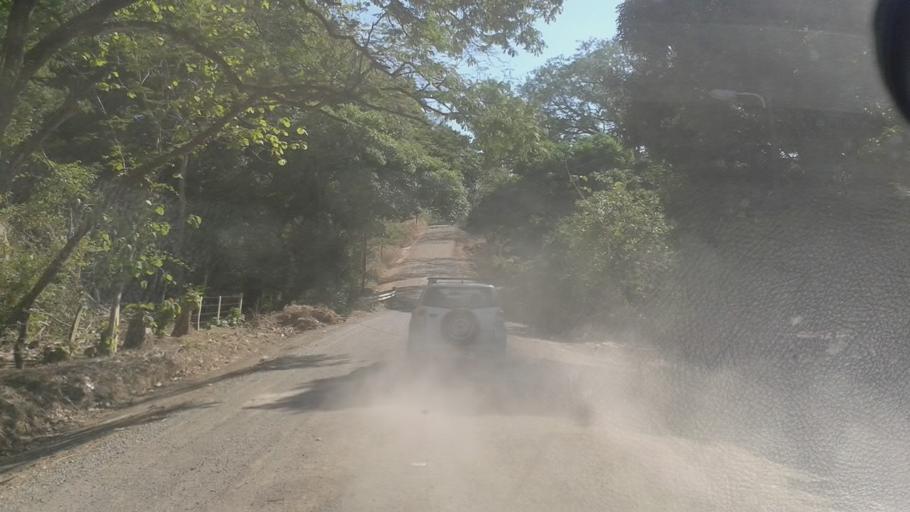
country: CR
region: Guanacaste
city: Santa Cruz
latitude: 10.1619
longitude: -85.7858
